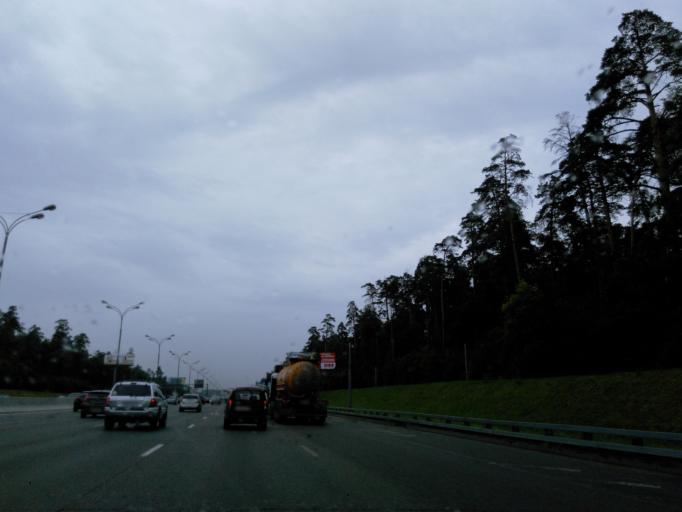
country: RU
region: Moscow
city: Rublevo
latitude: 55.7943
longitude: 37.3765
